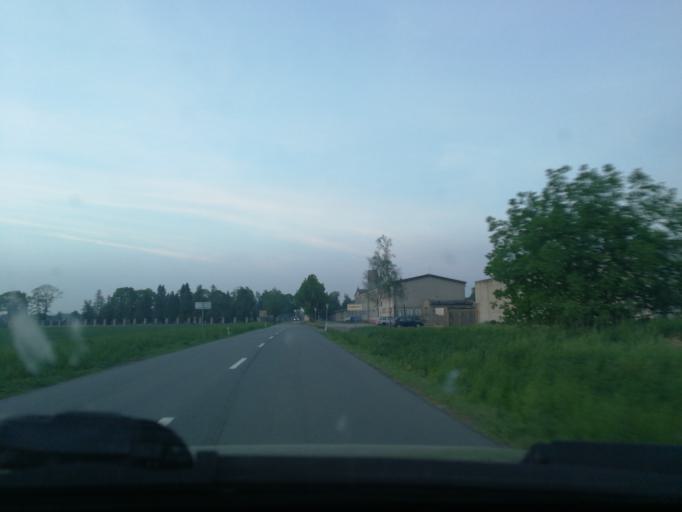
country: CZ
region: Zlin
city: Holesov
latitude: 49.3007
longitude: 17.5579
